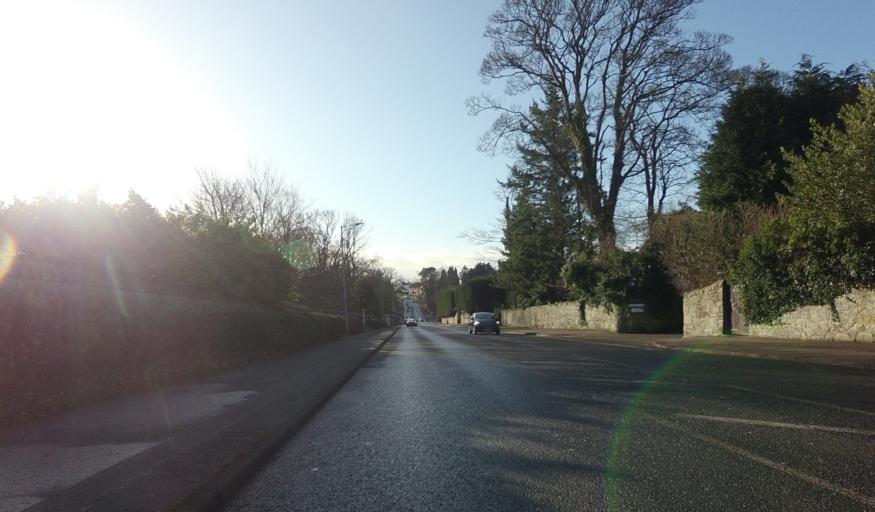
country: GB
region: Scotland
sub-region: Edinburgh
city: Currie
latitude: 55.9674
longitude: -3.3075
